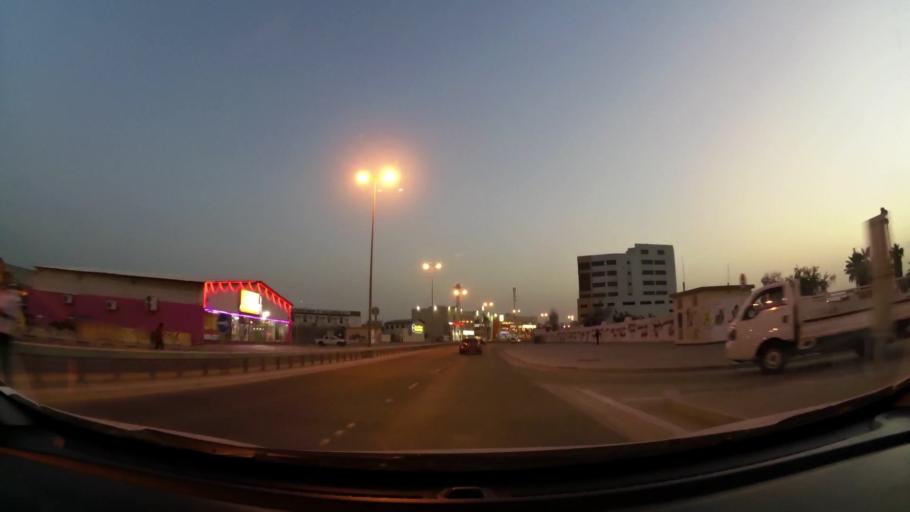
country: BH
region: Manama
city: Jidd Hafs
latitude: 26.2105
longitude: 50.5546
